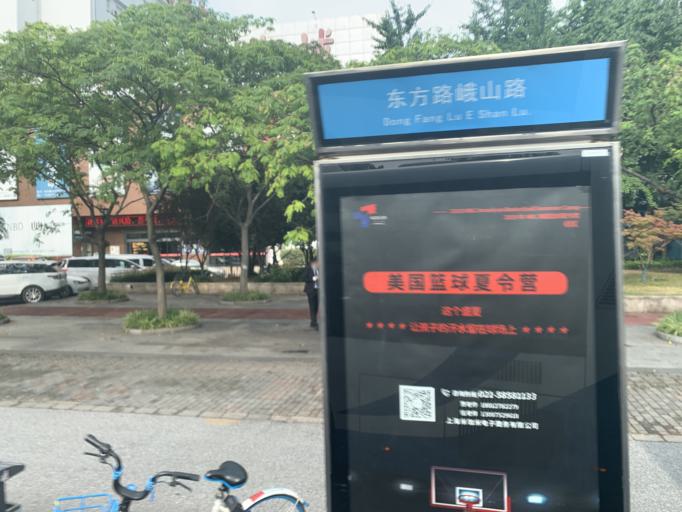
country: CN
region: Shanghai Shi
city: Pudong
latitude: 31.2186
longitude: 121.5253
